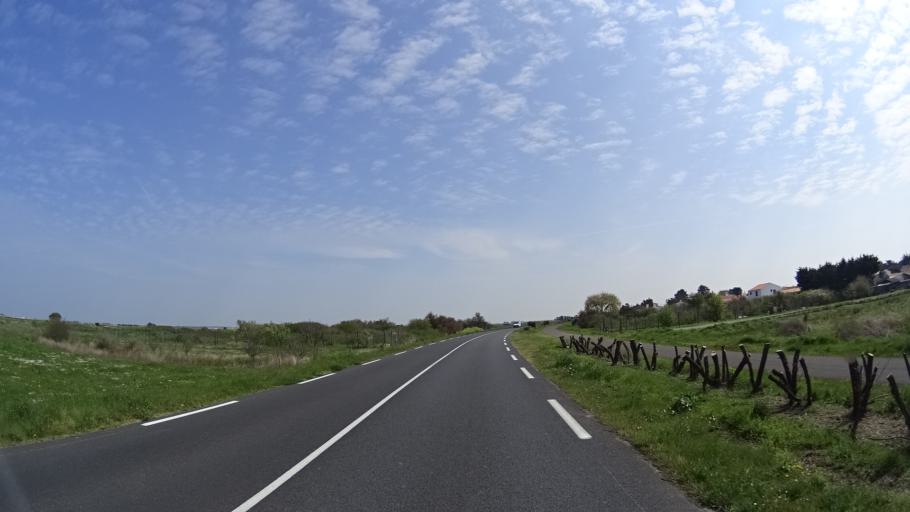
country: FR
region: Pays de la Loire
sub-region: Departement de la Vendee
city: La Gueriniere
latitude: 46.9883
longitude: -2.2851
